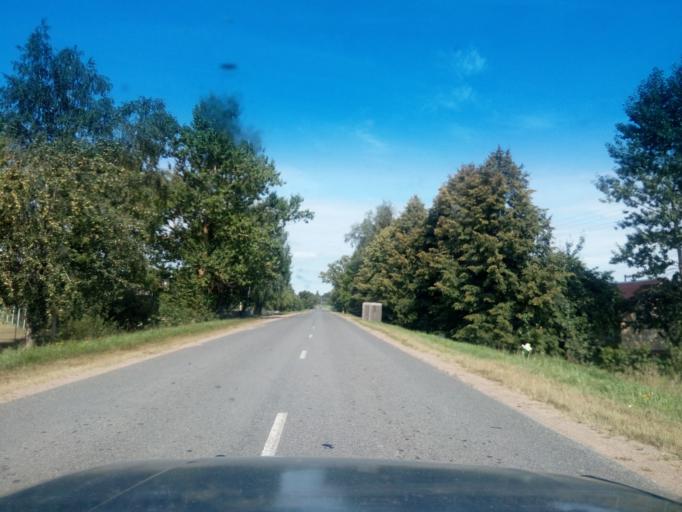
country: BY
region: Vitebsk
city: Vyerkhnyadzvinsk
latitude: 55.8259
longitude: 27.7353
